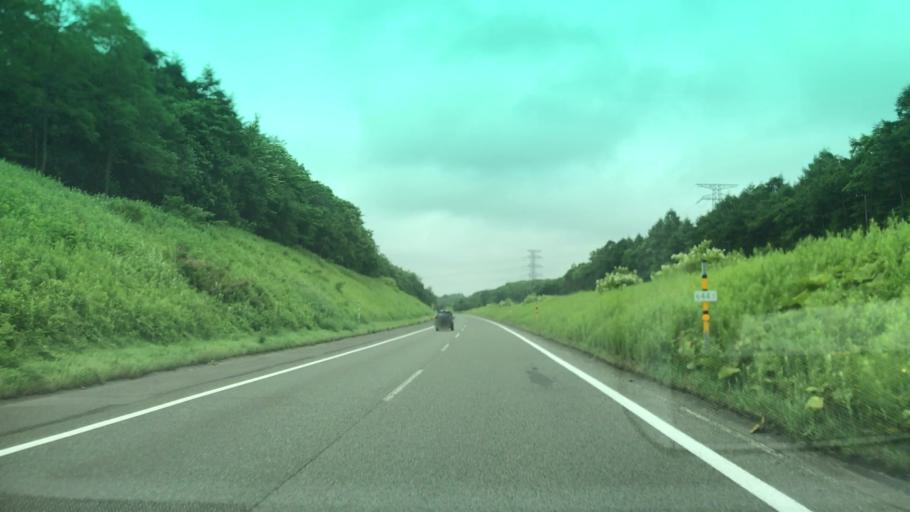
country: JP
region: Hokkaido
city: Chitose
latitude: 42.7323
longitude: 141.6528
